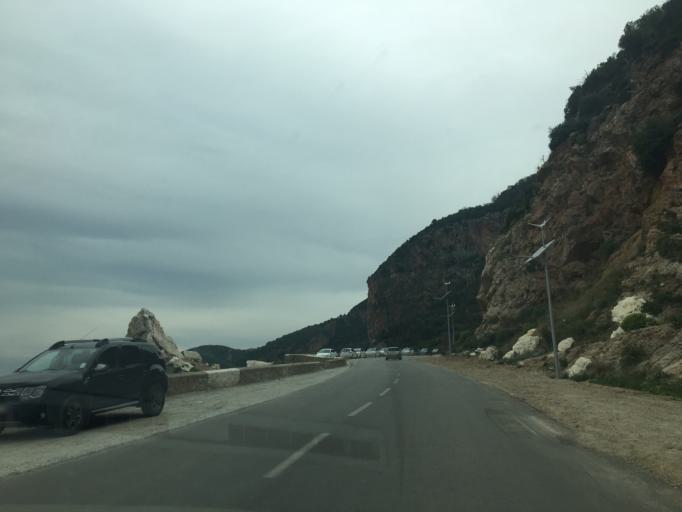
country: DZ
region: Tipaza
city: Tipasa
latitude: 36.6183
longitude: 2.4062
